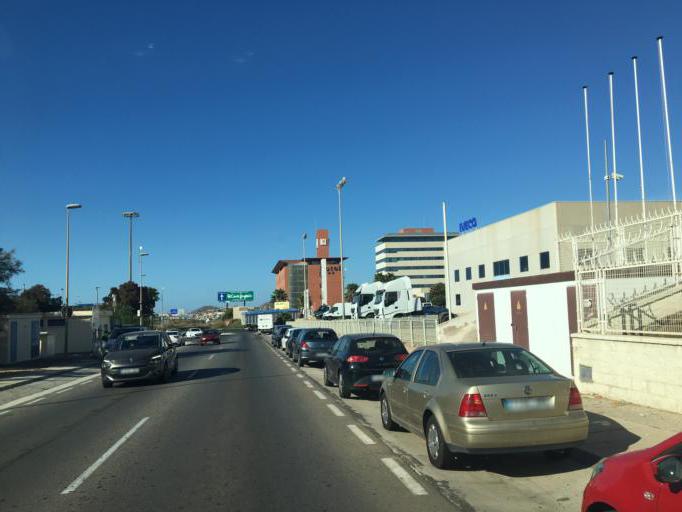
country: ES
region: Murcia
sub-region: Murcia
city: Cartagena
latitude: 37.6183
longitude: -0.9538
